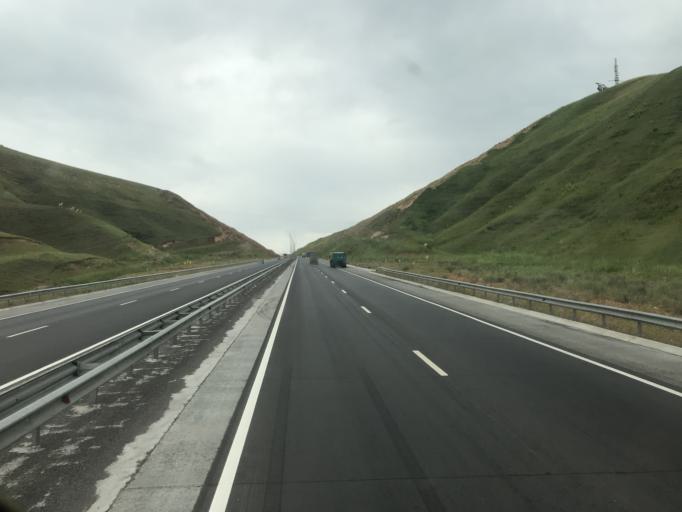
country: KZ
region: Ongtustik Qazaqstan
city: Qazyqurt
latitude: 42.0034
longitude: 69.4746
